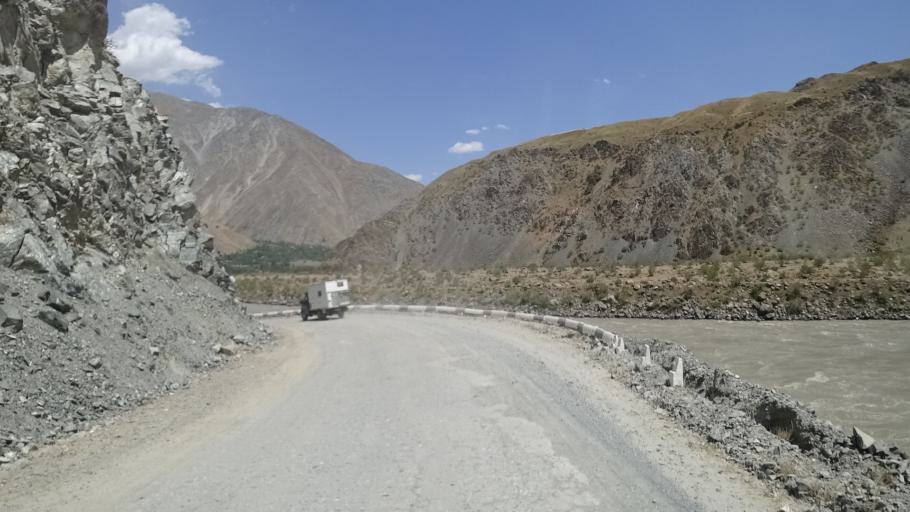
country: AF
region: Badakhshan
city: Nusay
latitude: 38.4643
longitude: 70.8660
